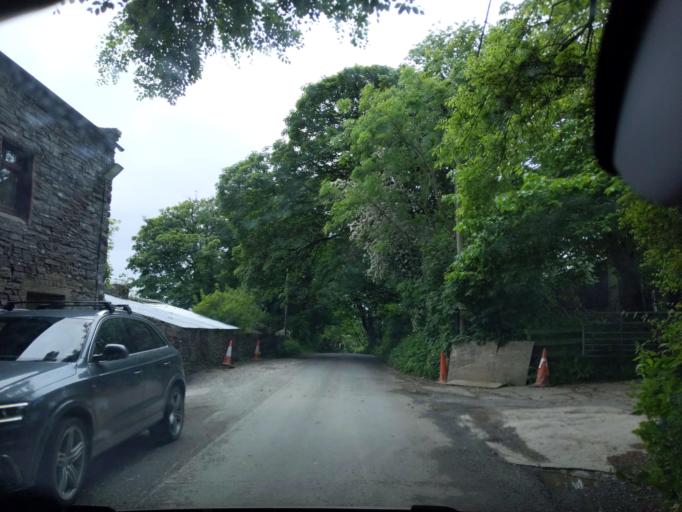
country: IM
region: Douglas
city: Douglas
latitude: 54.1455
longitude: -4.5628
